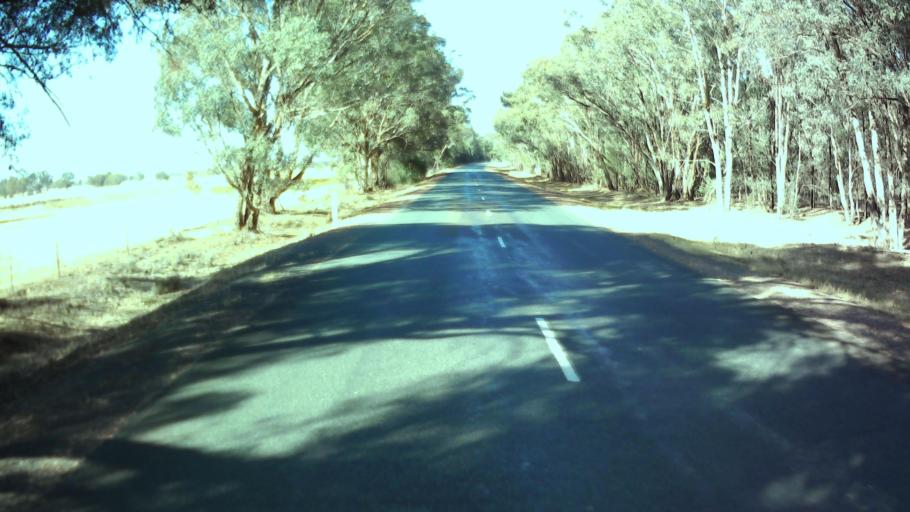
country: AU
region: New South Wales
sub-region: Weddin
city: Grenfell
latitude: -34.0110
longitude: 148.1179
